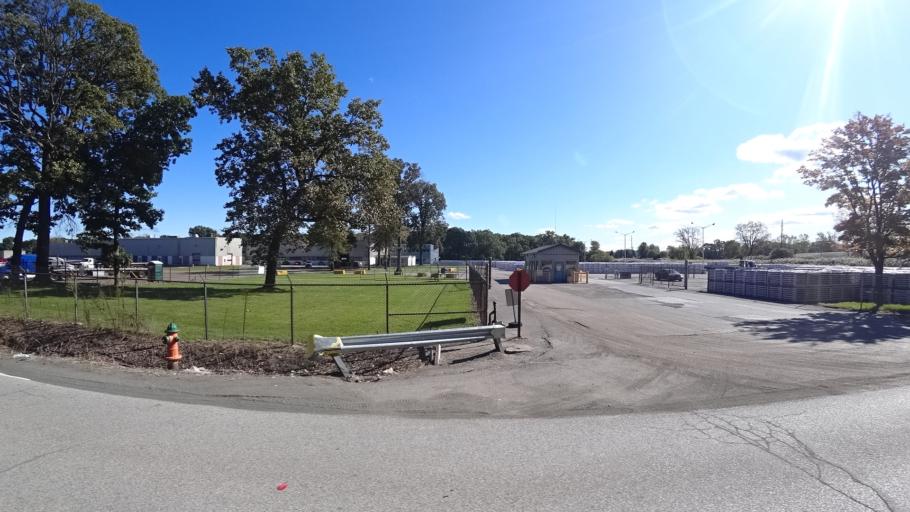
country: US
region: Indiana
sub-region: LaPorte County
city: Michigan City
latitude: 41.6817
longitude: -86.9133
